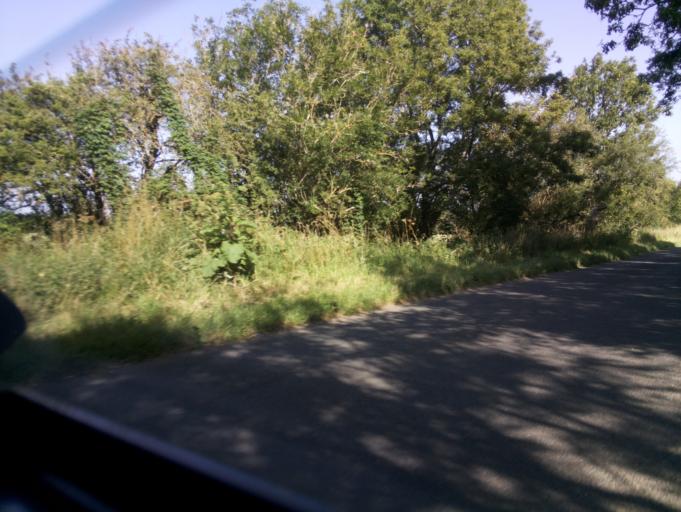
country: GB
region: England
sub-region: Oxfordshire
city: Bampton
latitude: 51.7107
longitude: -1.5224
